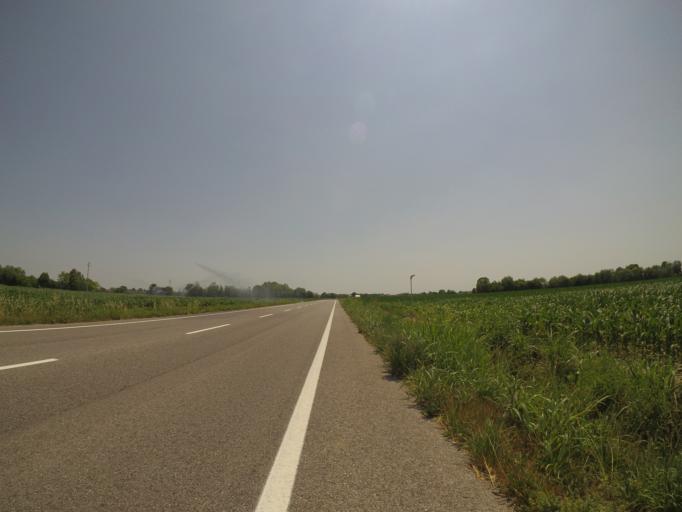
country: IT
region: Friuli Venezia Giulia
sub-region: Provincia di Udine
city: Varmo
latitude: 45.9032
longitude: 13.0047
